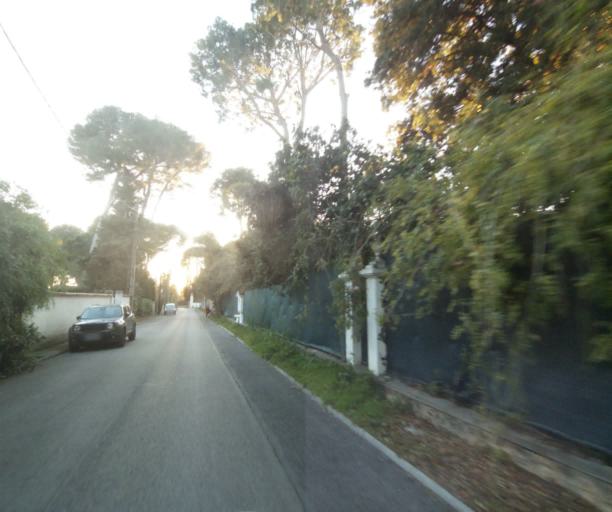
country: FR
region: Provence-Alpes-Cote d'Azur
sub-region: Departement des Alpes-Maritimes
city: Antibes
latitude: 43.5620
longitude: 7.1317
